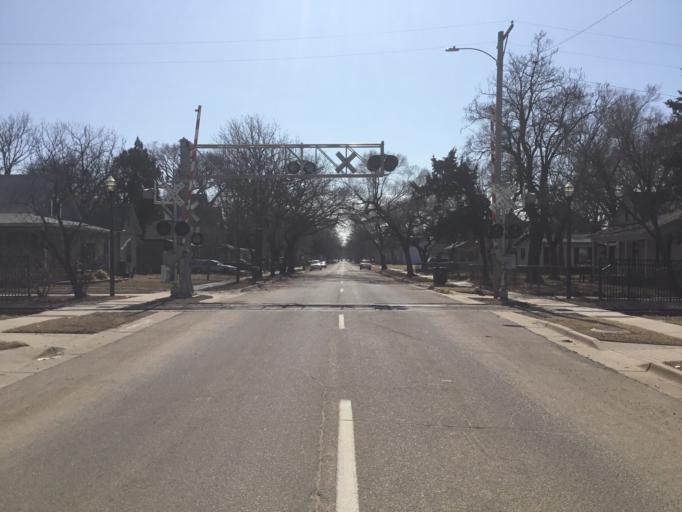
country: US
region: Kansas
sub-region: Sedgwick County
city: Wichita
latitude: 37.6700
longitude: -97.3329
